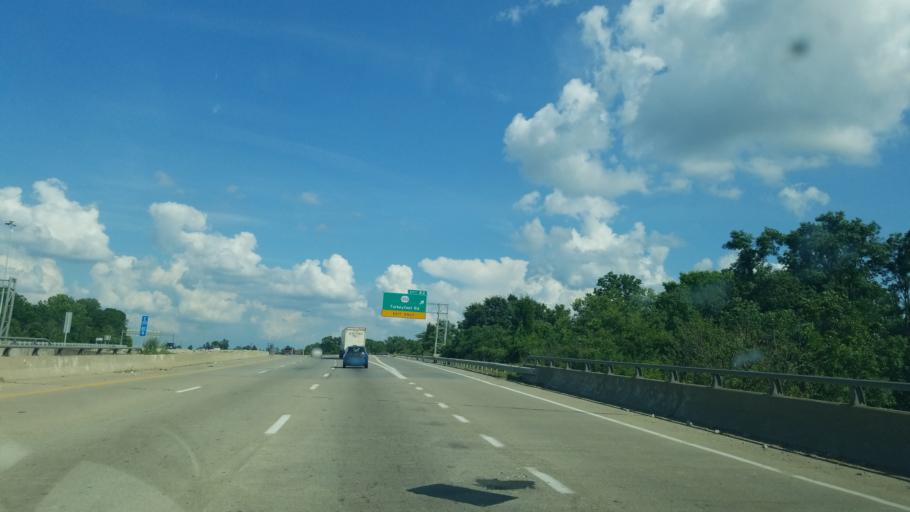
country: US
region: Kentucky
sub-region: Kenton County
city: Crestview Hills
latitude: 39.0284
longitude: -84.5777
